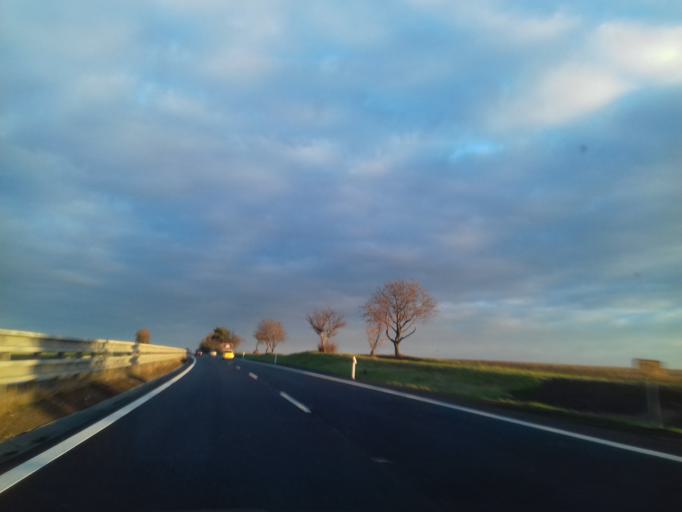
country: CZ
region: Olomoucky
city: Urcice
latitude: 49.4147
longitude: 17.1115
